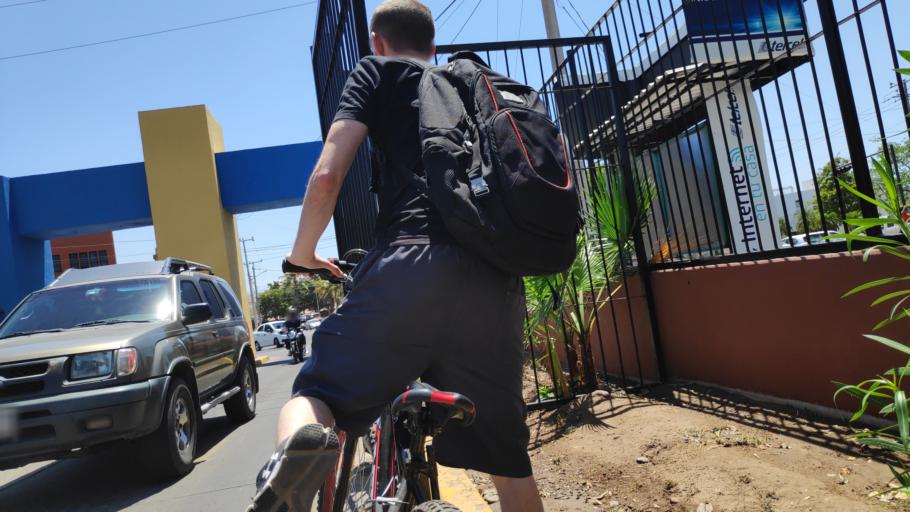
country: MX
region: Sinaloa
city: Culiacan
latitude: 24.8224
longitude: -107.3833
